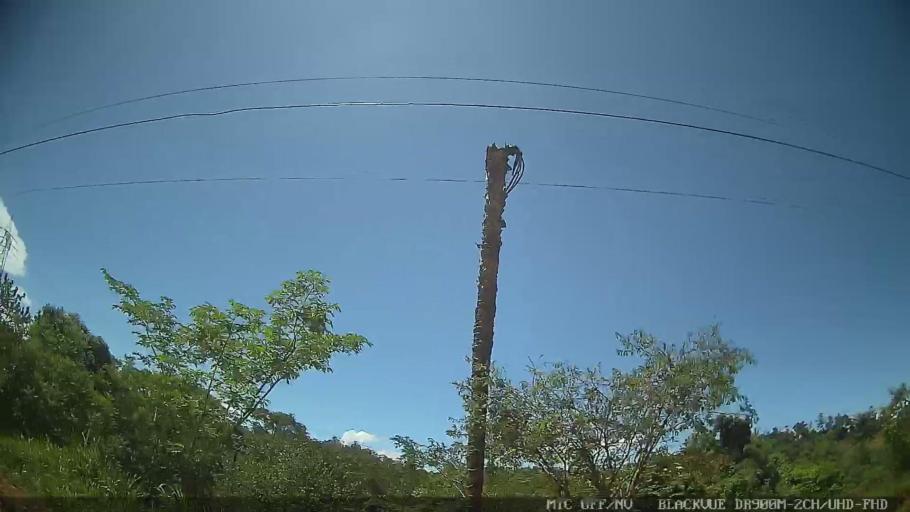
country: BR
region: Sao Paulo
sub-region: Pedreira
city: Pedreira
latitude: -22.7416
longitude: -46.9322
